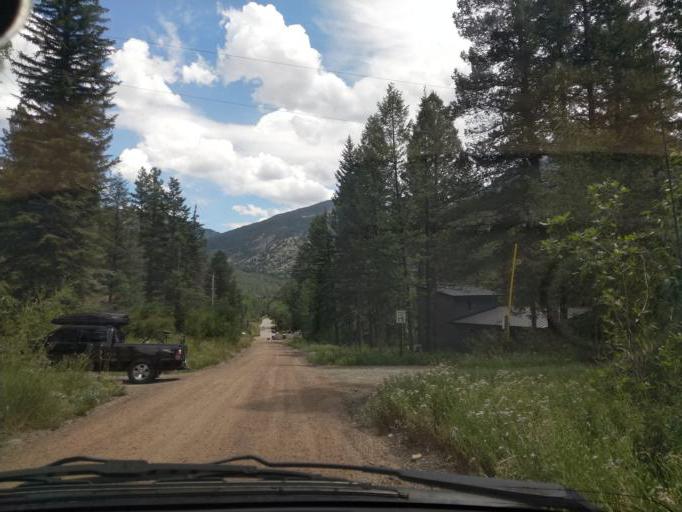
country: US
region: Colorado
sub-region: Gunnison County
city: Crested Butte
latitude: 39.0718
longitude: -107.1909
